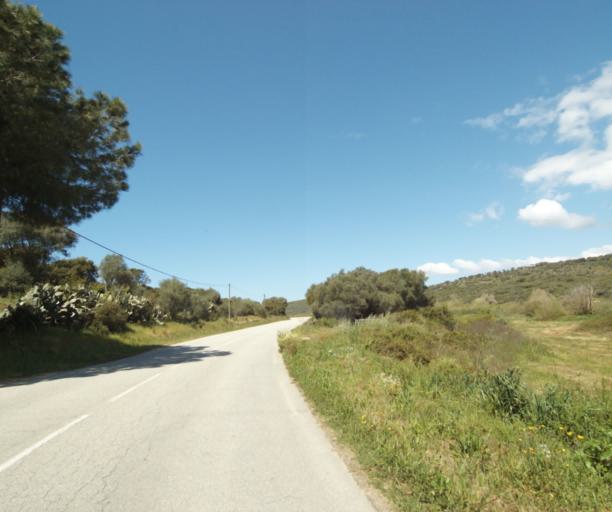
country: FR
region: Corsica
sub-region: Departement de la Corse-du-Sud
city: Propriano
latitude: 41.6579
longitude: 8.9006
